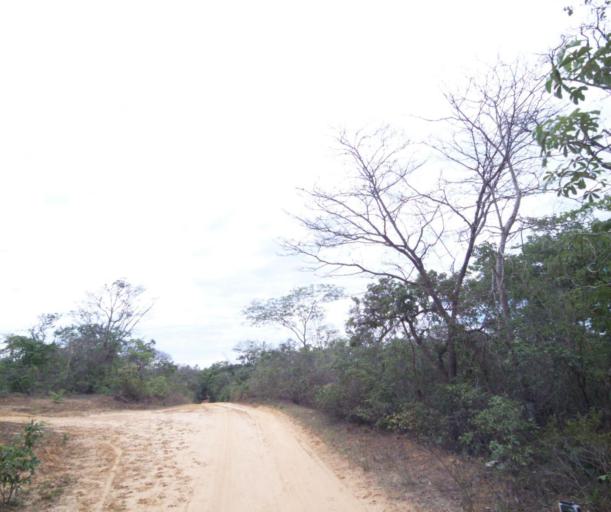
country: BR
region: Bahia
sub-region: Carinhanha
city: Carinhanha
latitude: -14.2499
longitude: -44.3719
